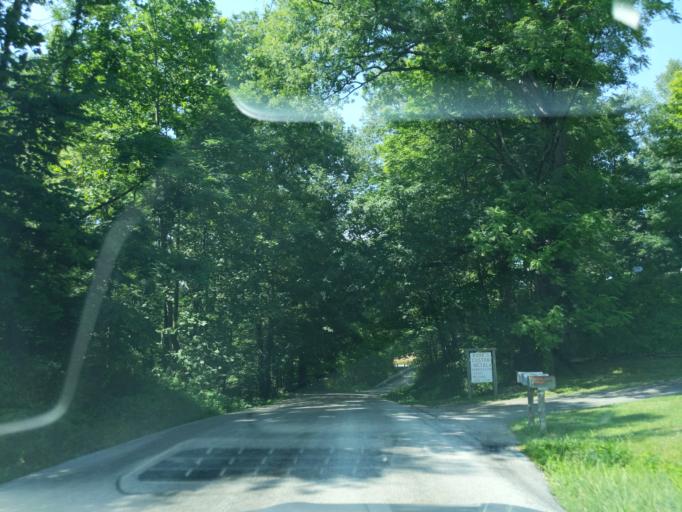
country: US
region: Indiana
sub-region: Ripley County
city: Osgood
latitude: 39.1102
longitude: -85.3438
